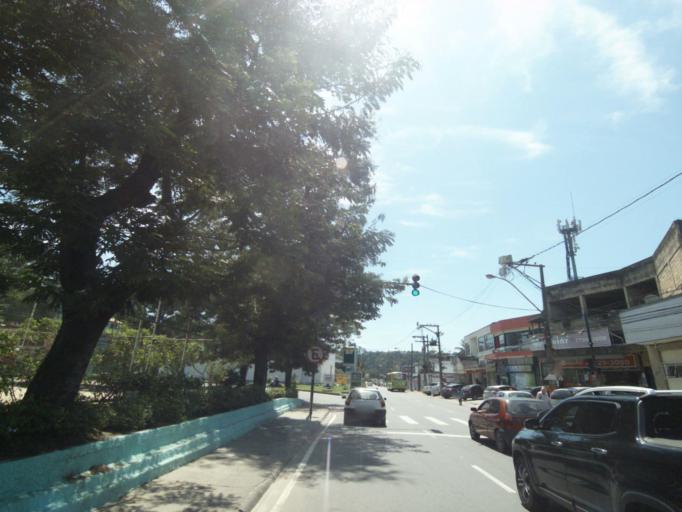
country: BR
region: Rio de Janeiro
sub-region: Sao Goncalo
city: Sao Goncalo
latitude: -22.8780
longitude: -43.0262
